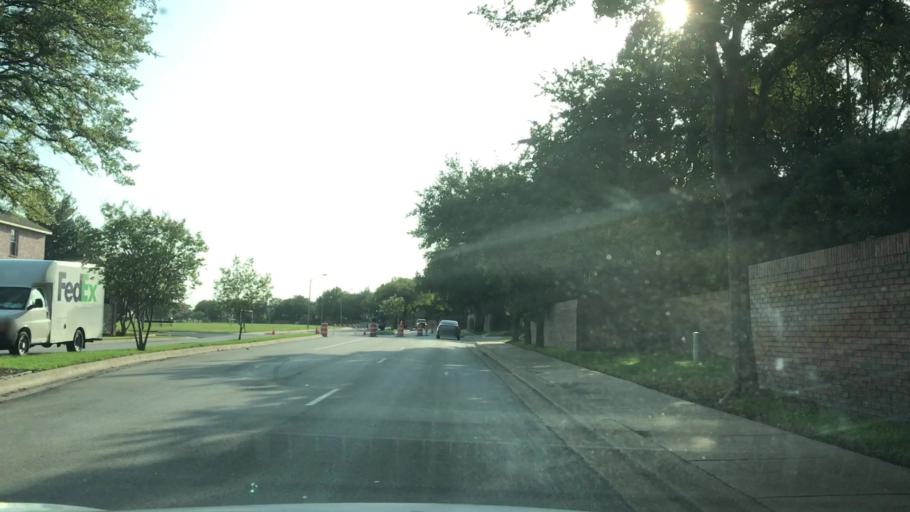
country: US
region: Texas
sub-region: Tarrant County
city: Euless
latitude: 32.8465
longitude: -97.0747
